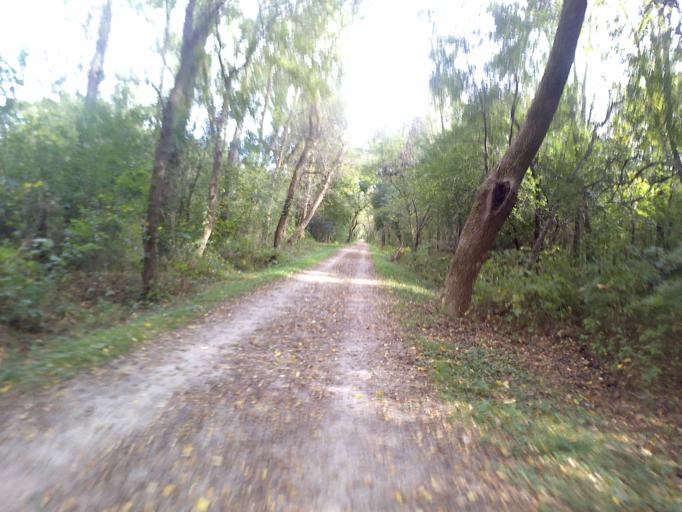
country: US
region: Illinois
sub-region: DuPage County
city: Winfield
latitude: 41.8974
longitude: -88.1695
